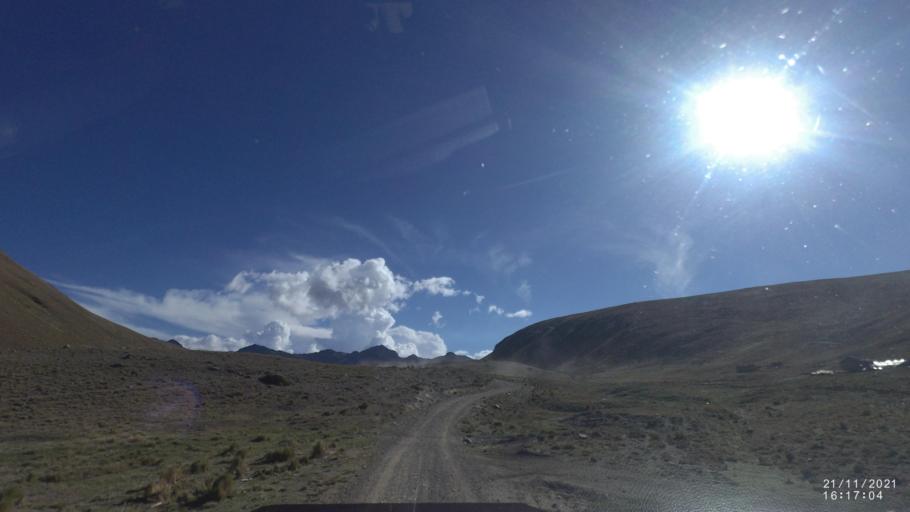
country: BO
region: Cochabamba
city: Cochabamba
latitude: -17.0019
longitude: -66.2809
